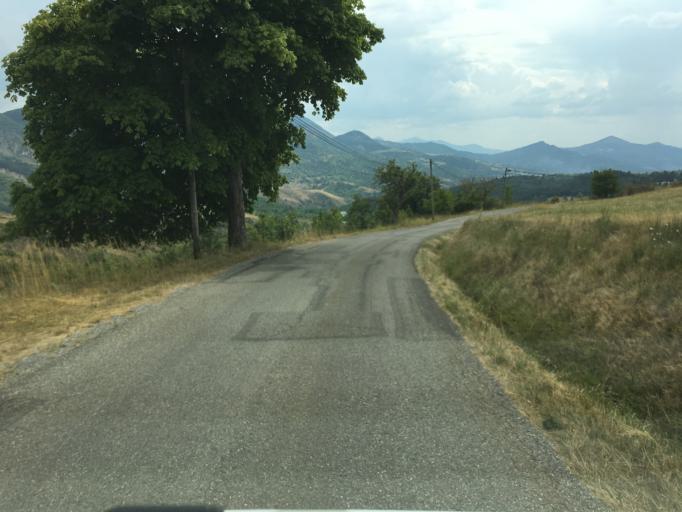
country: FR
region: Provence-Alpes-Cote d'Azur
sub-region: Departement des Alpes-de-Haute-Provence
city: Digne-les-Bains
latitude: 44.1886
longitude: 6.1419
